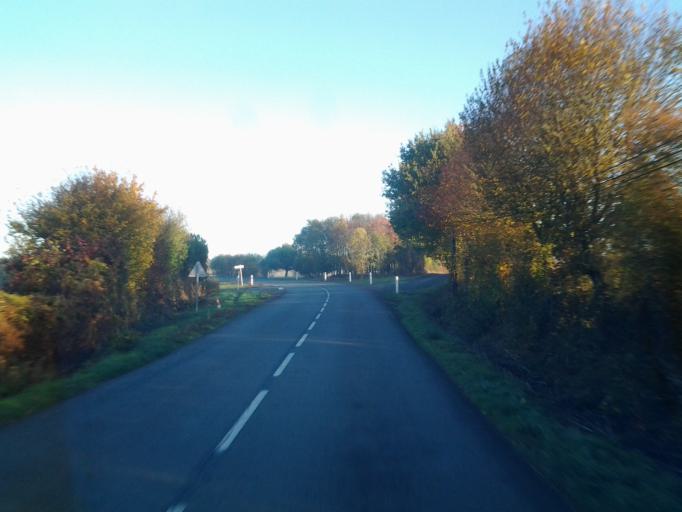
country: FR
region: Pays de la Loire
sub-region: Departement de la Vendee
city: Bournezeau
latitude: 46.6499
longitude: -1.2296
